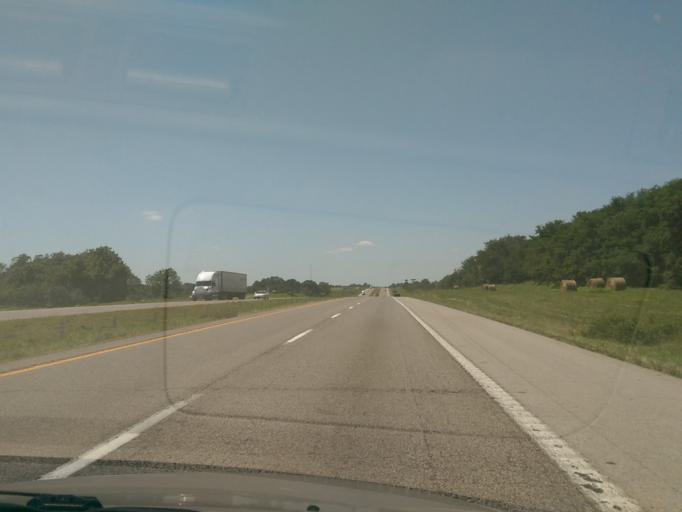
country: US
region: Missouri
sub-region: Saline County
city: Marshall
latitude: 38.9520
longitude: -93.0702
